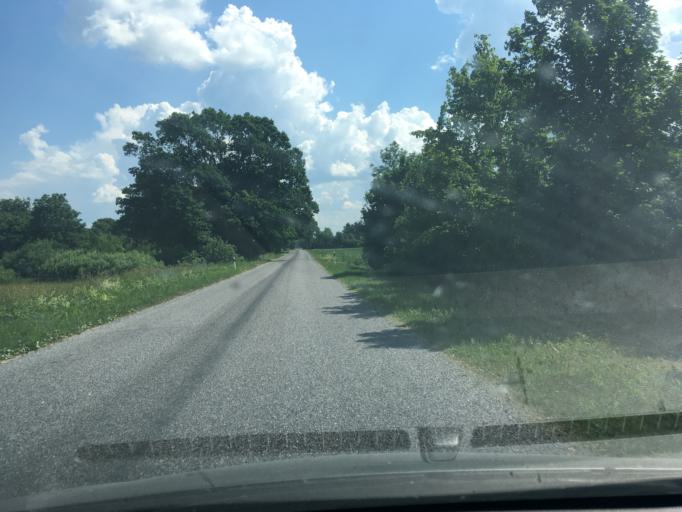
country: EE
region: Laeaene
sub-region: Lihula vald
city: Lihula
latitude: 58.7123
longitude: 24.0065
